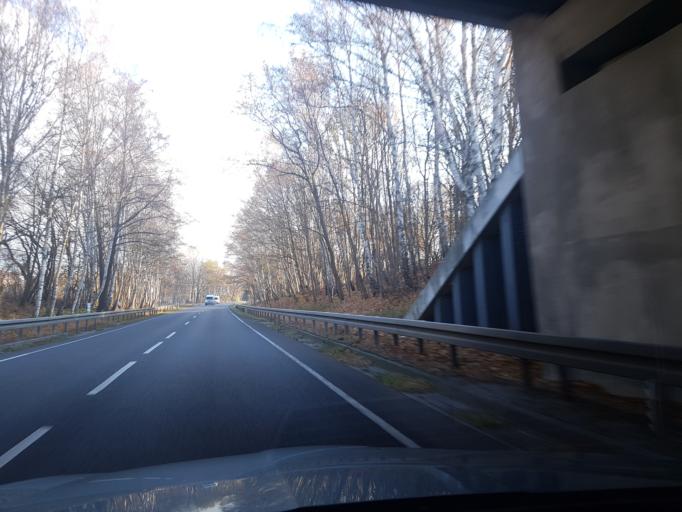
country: DE
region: Brandenburg
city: Luckau
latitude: 51.8291
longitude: 13.6280
